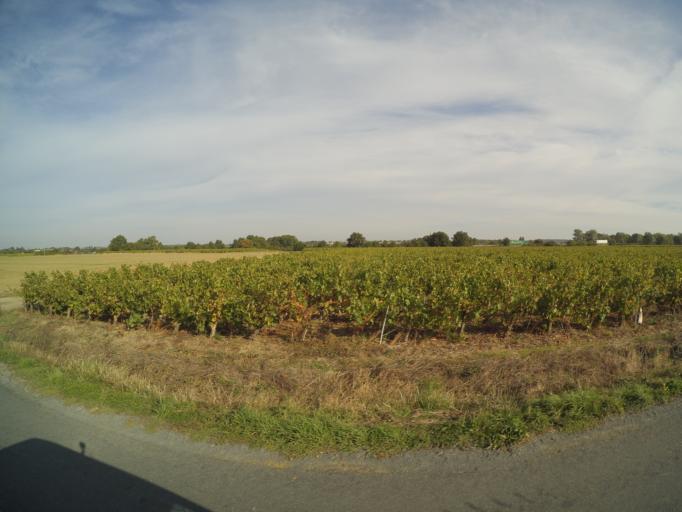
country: FR
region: Pays de la Loire
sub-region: Departement de Maine-et-Loire
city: Tillieres
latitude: 47.1377
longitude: -1.1703
